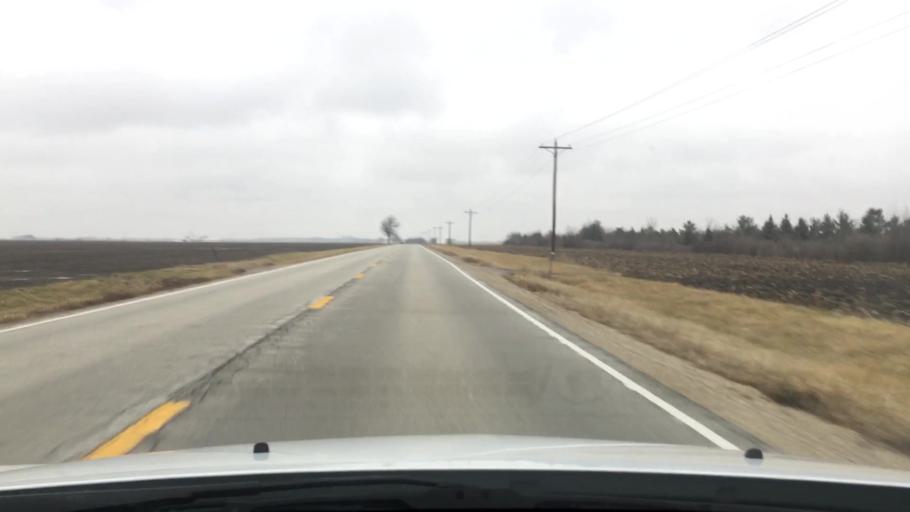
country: US
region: Illinois
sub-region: Iroquois County
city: Clifton
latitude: 40.8871
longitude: -87.8751
